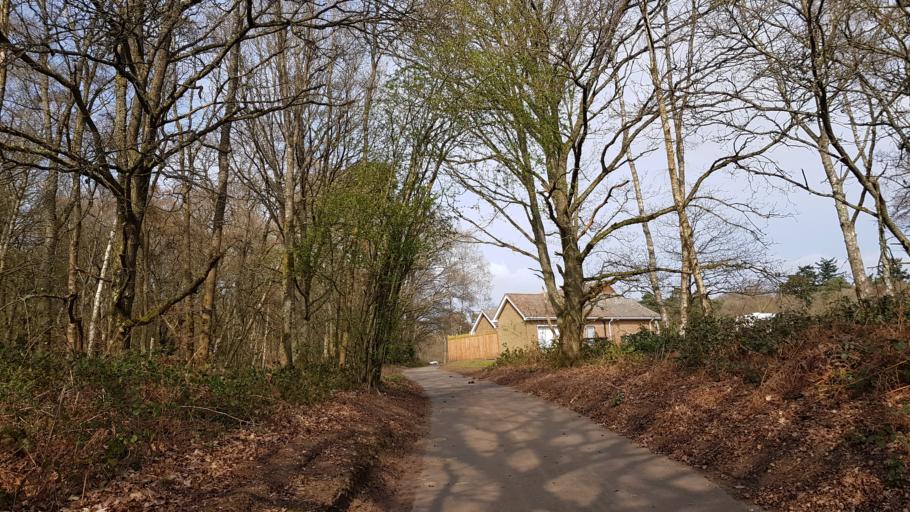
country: GB
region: England
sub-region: Surrey
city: Chilworth
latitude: 51.2112
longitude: -0.4866
